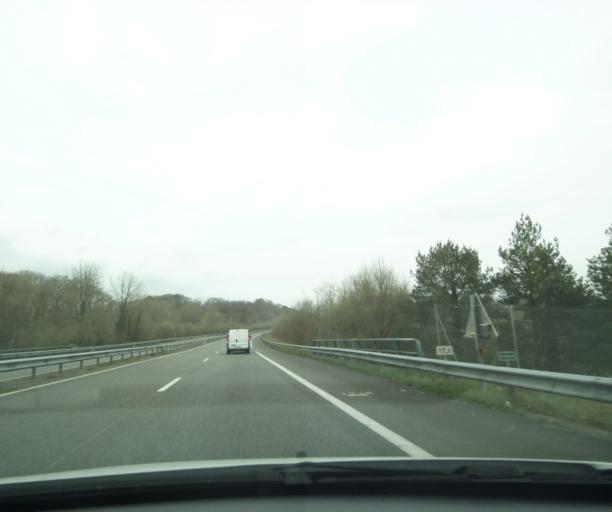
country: FR
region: Aquitaine
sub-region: Departement des Pyrenees-Atlantiques
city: Urt
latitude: 43.4774
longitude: -1.2770
